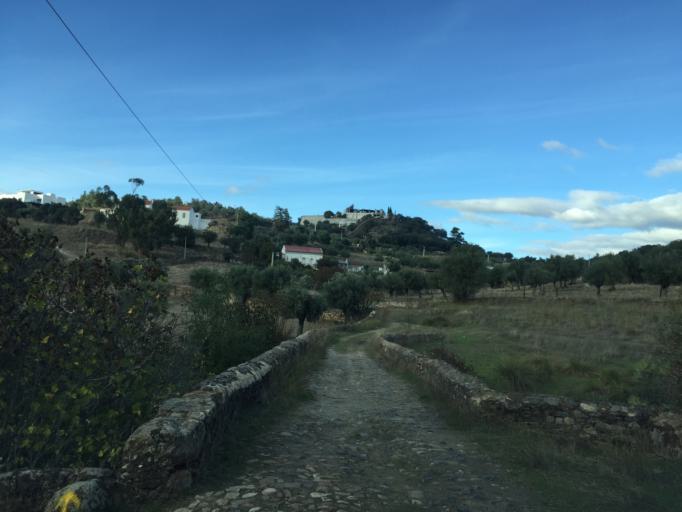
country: PT
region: Portalegre
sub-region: Alter do Chao
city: Alter do Chao
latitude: 39.2795
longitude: -7.6424
